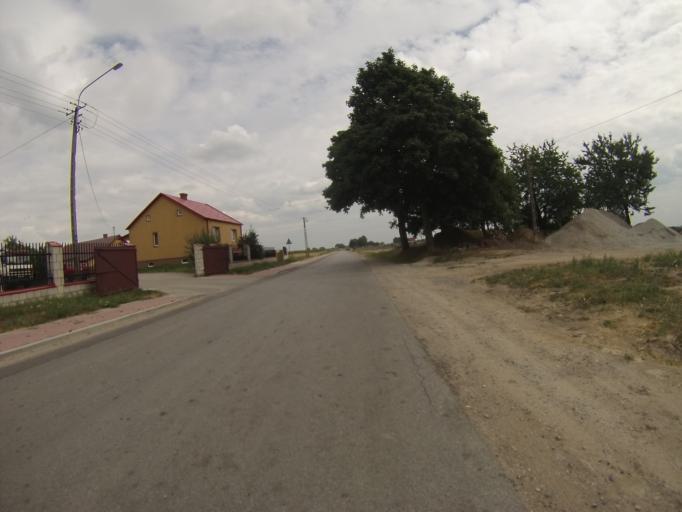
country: PL
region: Swietokrzyskie
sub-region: Powiat kielecki
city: Lagow
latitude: 50.7306
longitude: 21.1015
